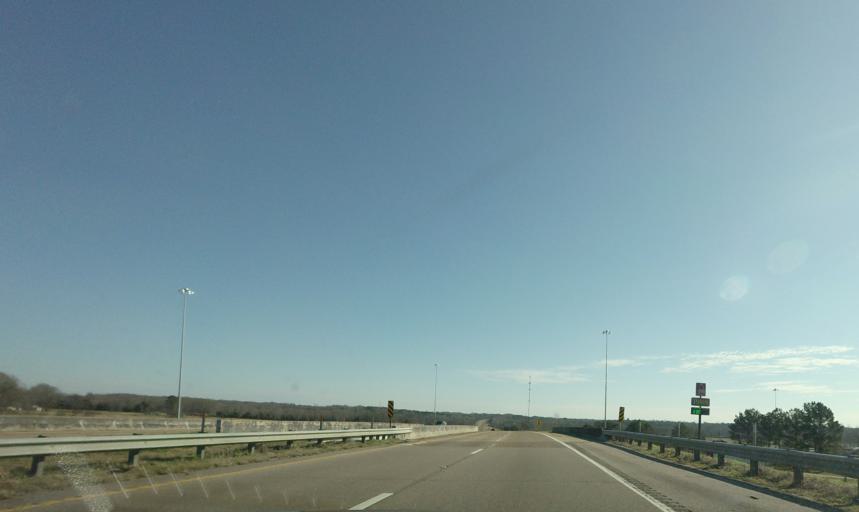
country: US
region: Mississippi
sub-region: Union County
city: New Albany
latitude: 34.4699
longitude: -89.0070
